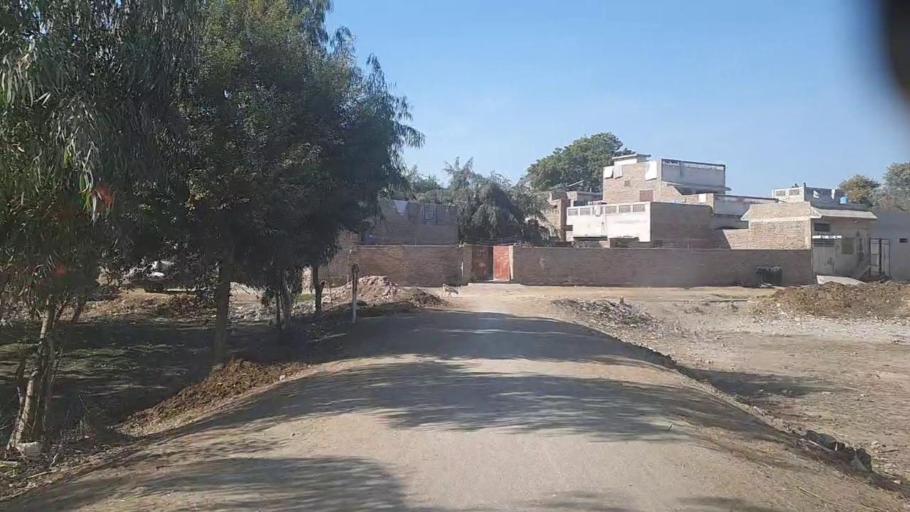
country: PK
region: Sindh
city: Khairpur
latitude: 28.0664
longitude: 69.6501
